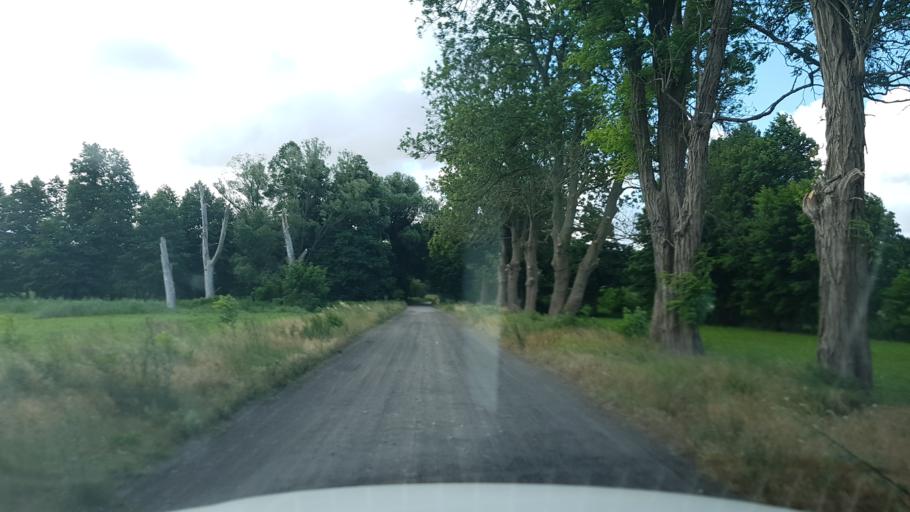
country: PL
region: West Pomeranian Voivodeship
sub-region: Powiat mysliborski
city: Debno
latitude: 52.7145
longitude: 14.6560
